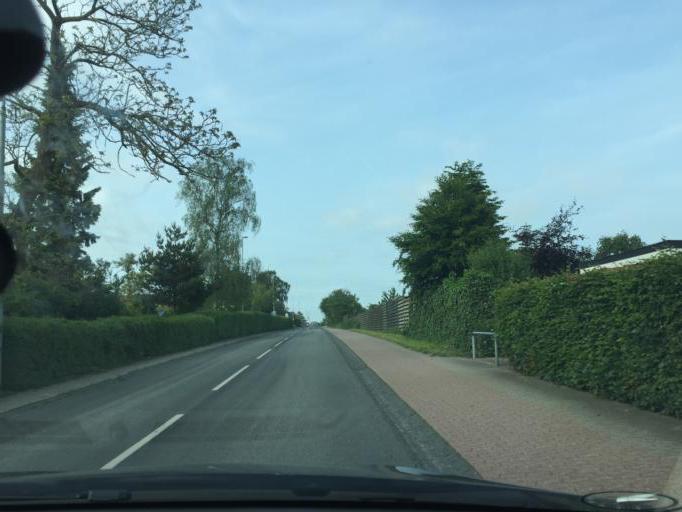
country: DK
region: South Denmark
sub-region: Odense Kommune
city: Bellinge
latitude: 55.3342
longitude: 10.3235
